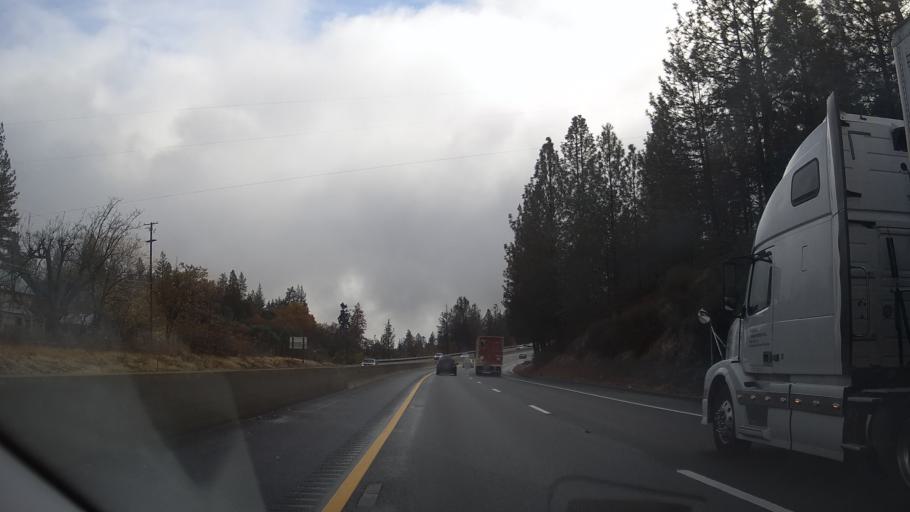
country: US
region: California
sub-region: Placer County
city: Meadow Vista
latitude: 39.0411
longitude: -120.9737
